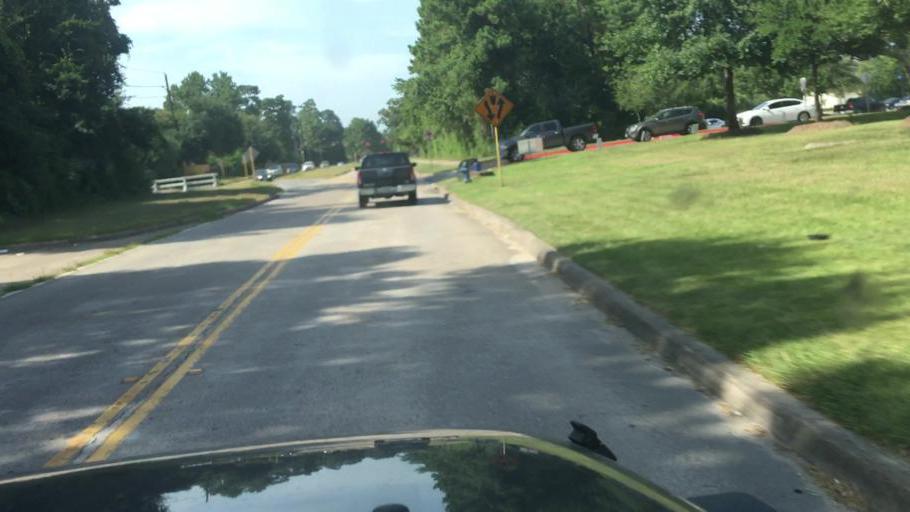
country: US
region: Texas
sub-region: Harris County
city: Atascocita
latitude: 29.9959
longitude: -95.1782
